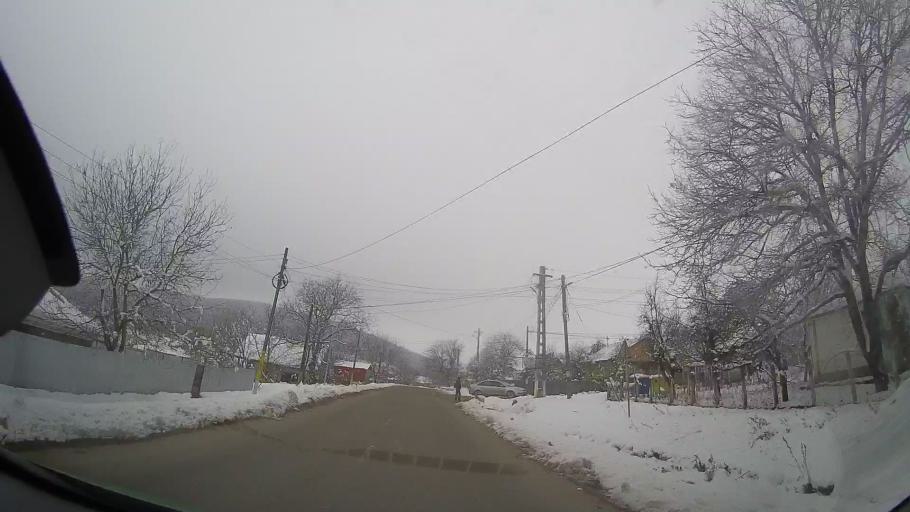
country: RO
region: Neamt
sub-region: Comuna Oniceni
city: Oniceni
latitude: 46.8000
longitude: 27.1485
